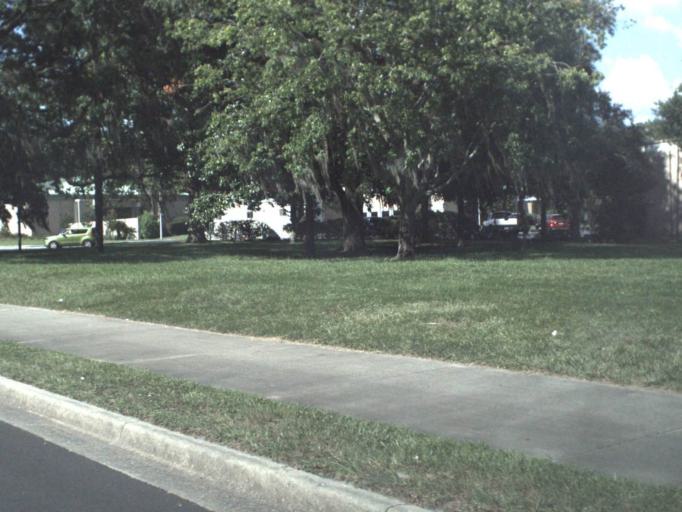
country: US
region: Florida
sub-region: Alachua County
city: Gainesville
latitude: 29.6335
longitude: -82.3724
